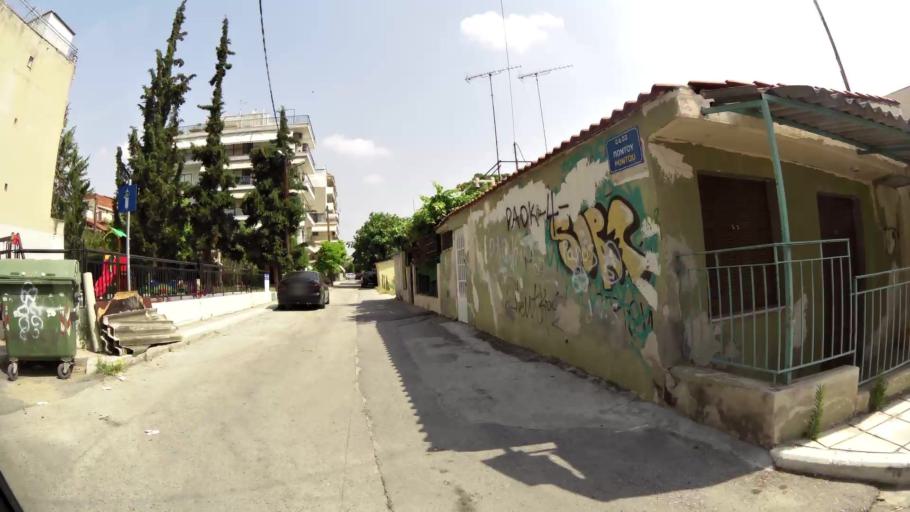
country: GR
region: Central Macedonia
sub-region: Nomos Thessalonikis
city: Stavroupoli
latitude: 40.6749
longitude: 22.9319
